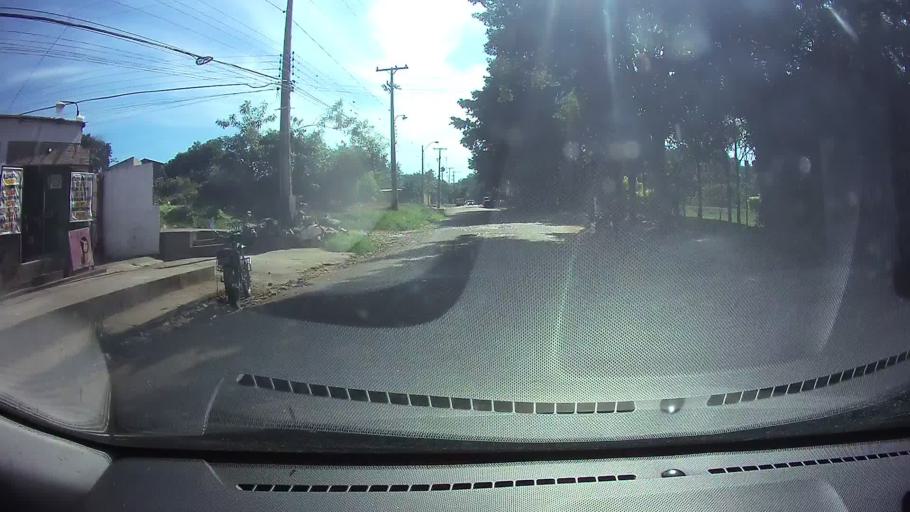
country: PY
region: Central
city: Villa Elisa
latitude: -25.3638
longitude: -57.5690
